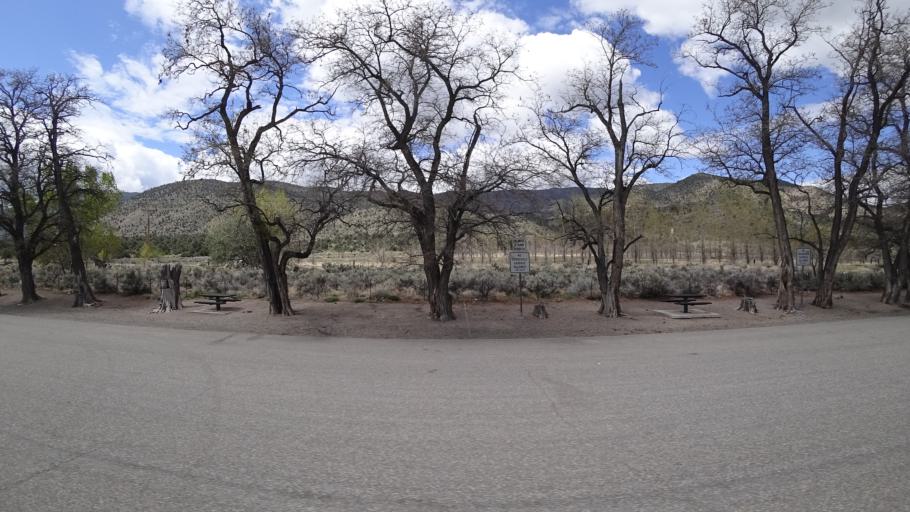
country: US
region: Nevada
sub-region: Douglas County
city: Gardnerville Ranchos
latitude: 38.7486
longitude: -119.5681
